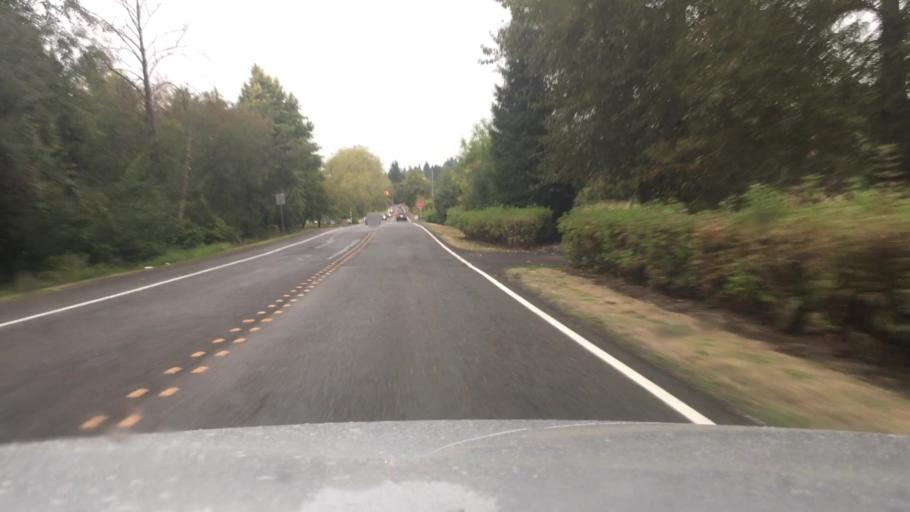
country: US
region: Washington
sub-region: King County
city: Eastgate
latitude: 47.5949
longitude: -122.1318
